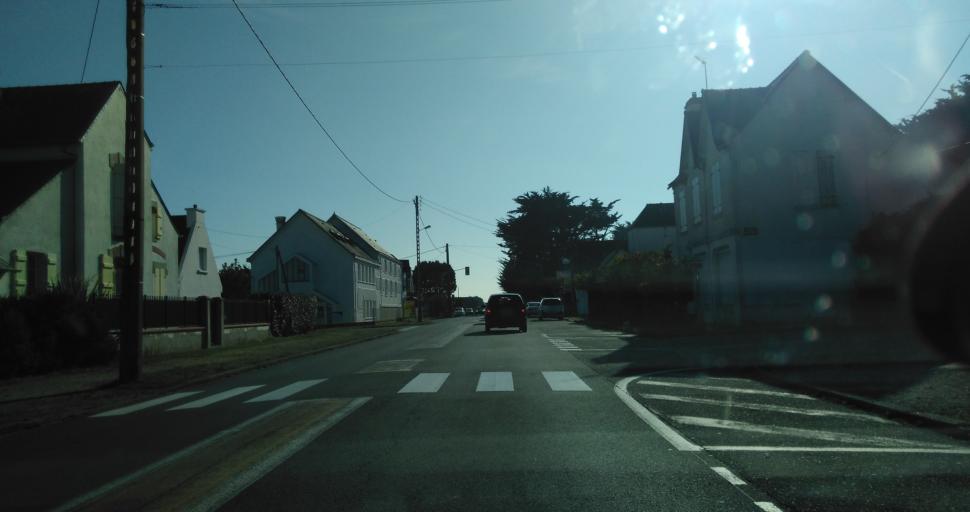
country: FR
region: Brittany
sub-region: Departement du Morbihan
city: Saint-Pierre-Quiberon
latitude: 47.5585
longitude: -3.1344
